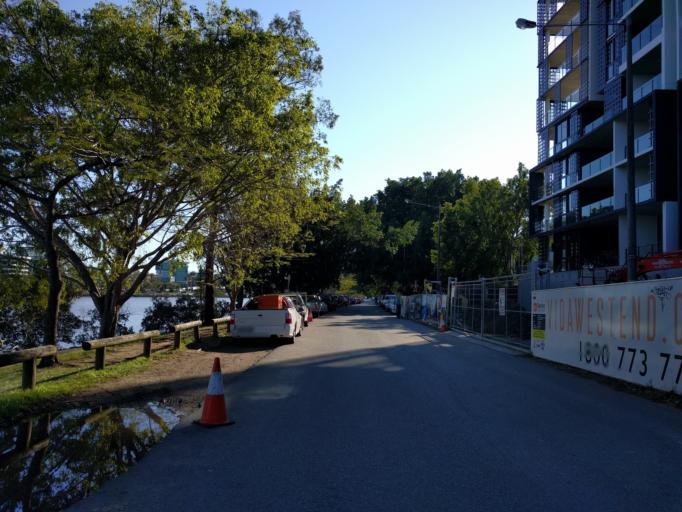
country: AU
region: Queensland
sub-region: Brisbane
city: Milton
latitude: -27.4757
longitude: 153.0060
